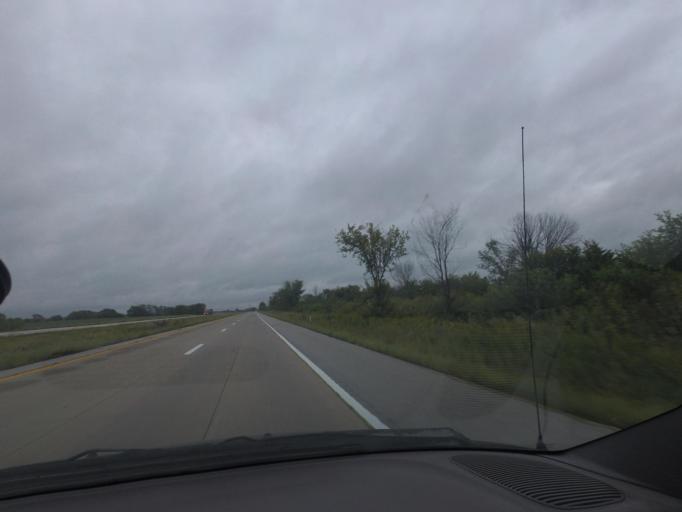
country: US
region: Missouri
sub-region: Marion County
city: Monroe City
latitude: 39.6605
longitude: -91.8202
